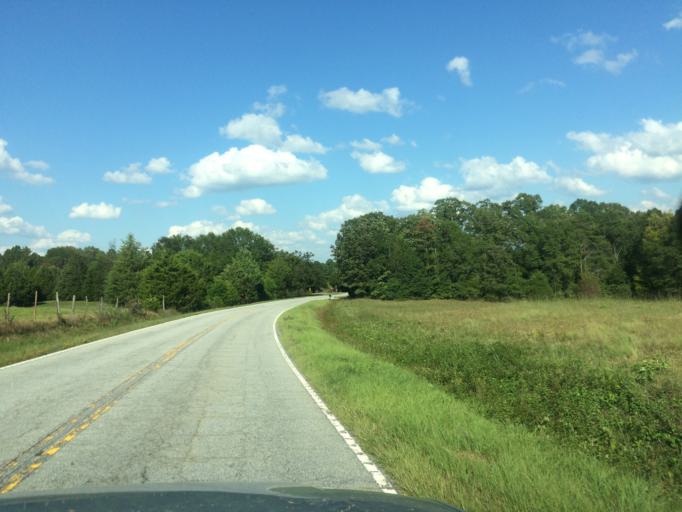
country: US
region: South Carolina
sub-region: Greenwood County
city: Ware Shoals
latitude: 34.4471
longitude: -82.2099
